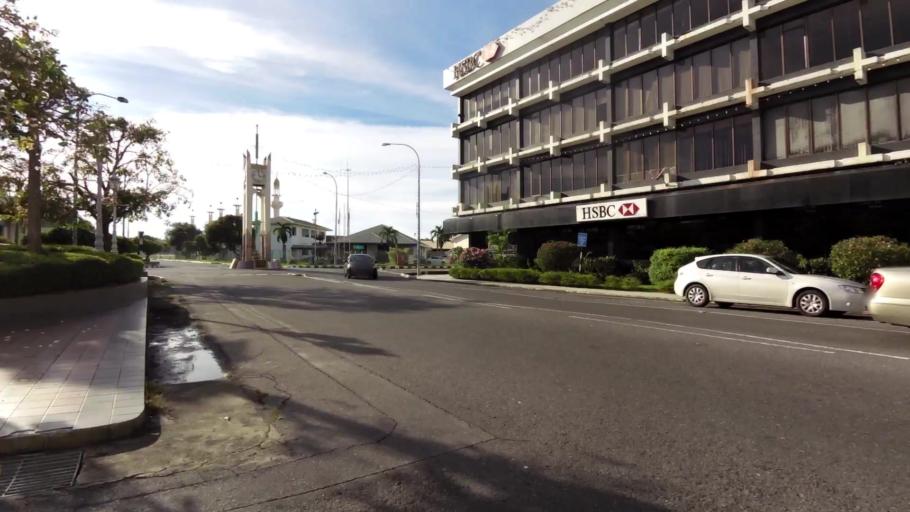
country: BN
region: Belait
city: Kuala Belait
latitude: 4.5840
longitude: 114.1919
